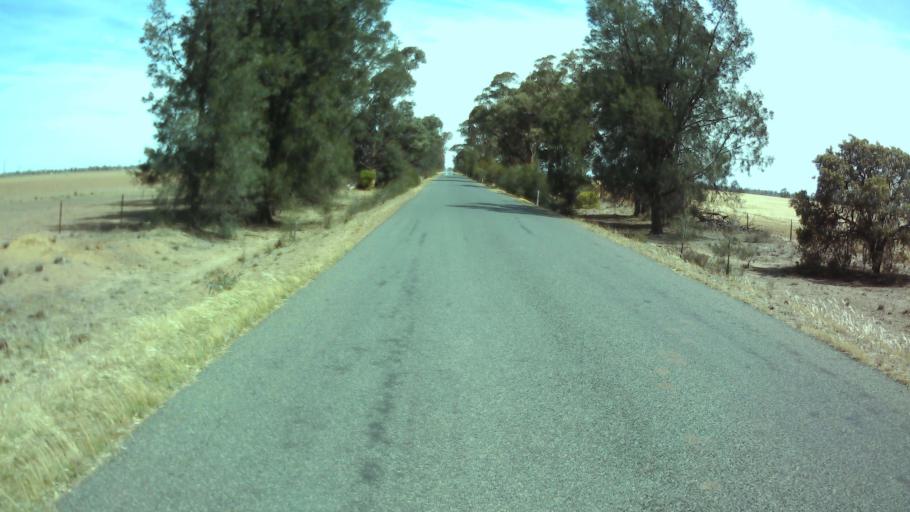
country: AU
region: New South Wales
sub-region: Weddin
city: Grenfell
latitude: -33.9728
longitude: 147.7795
